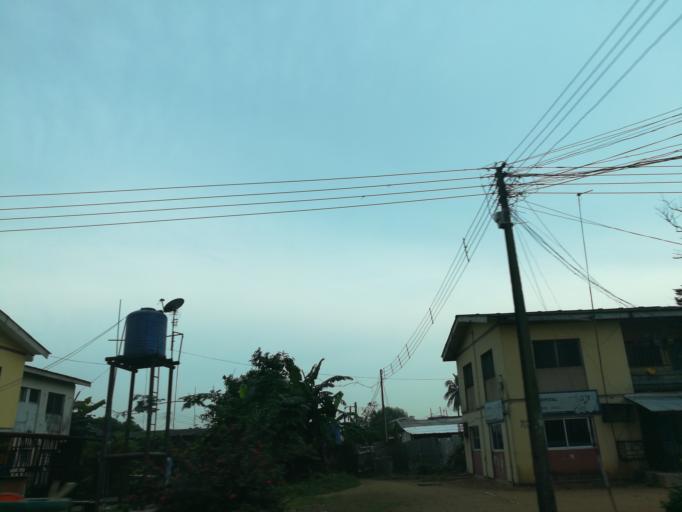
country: NG
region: Rivers
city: Port Harcourt
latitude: 4.8242
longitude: 7.0272
